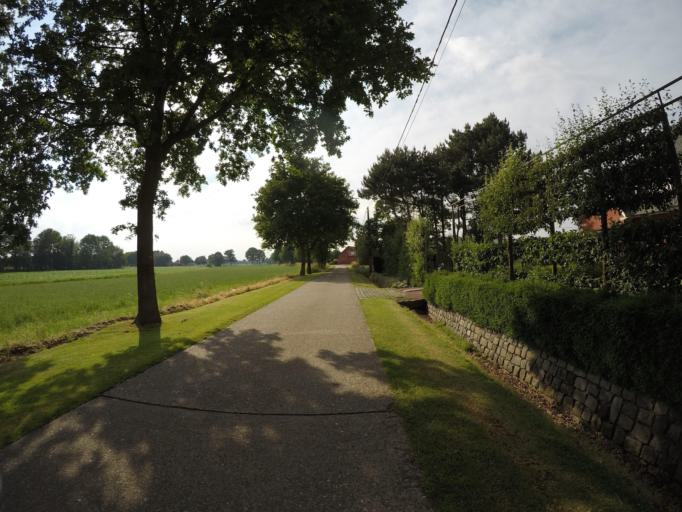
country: BE
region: Flanders
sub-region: Provincie Antwerpen
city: Brecht
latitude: 51.3676
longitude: 4.6947
